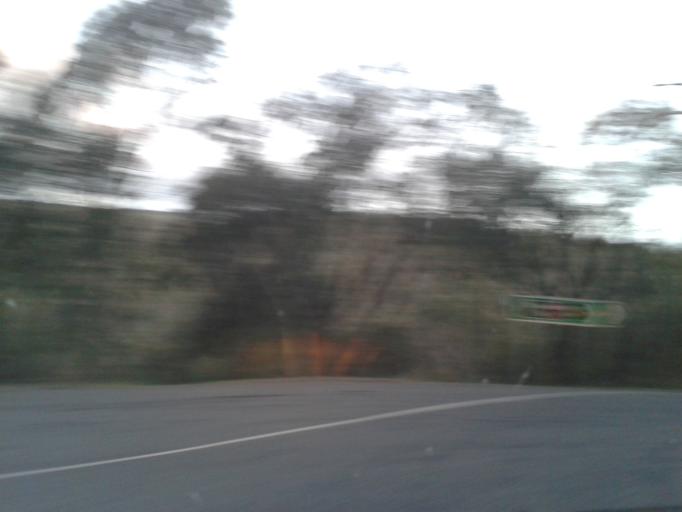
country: AU
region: Victoria
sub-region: Northern Grampians
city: Stawell
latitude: -37.1587
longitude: 142.4975
